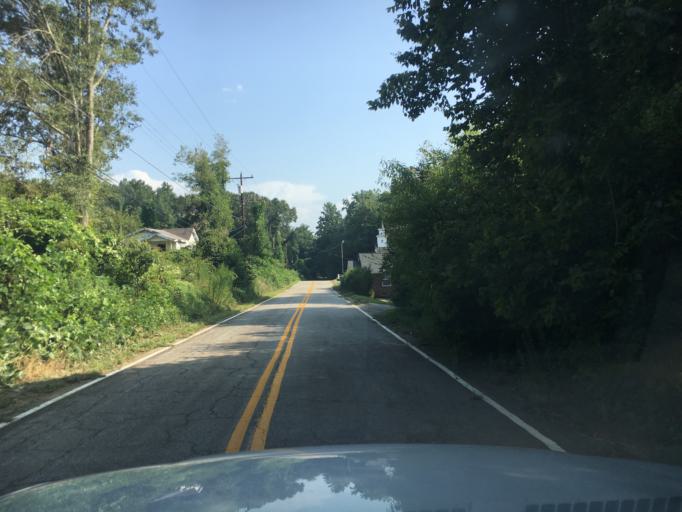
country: US
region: South Carolina
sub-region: Spartanburg County
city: Duncan
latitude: 34.9358
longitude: -82.1424
